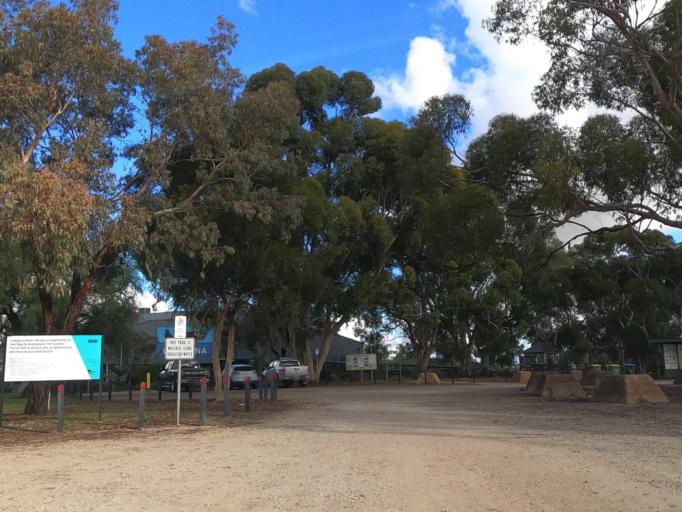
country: AU
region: Victoria
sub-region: Swan Hill
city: Swan Hill
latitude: -35.4501
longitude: 143.6275
